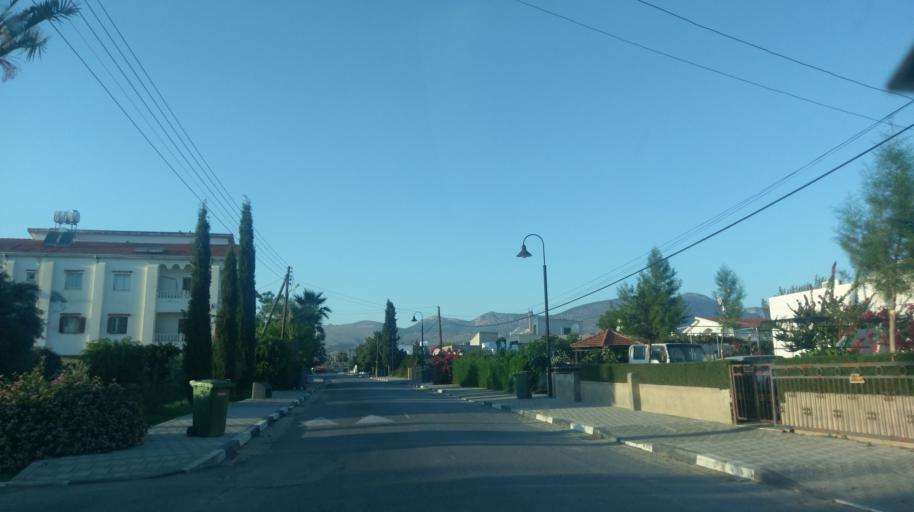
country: CY
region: Lefkosia
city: Geri
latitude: 35.2240
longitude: 33.5146
